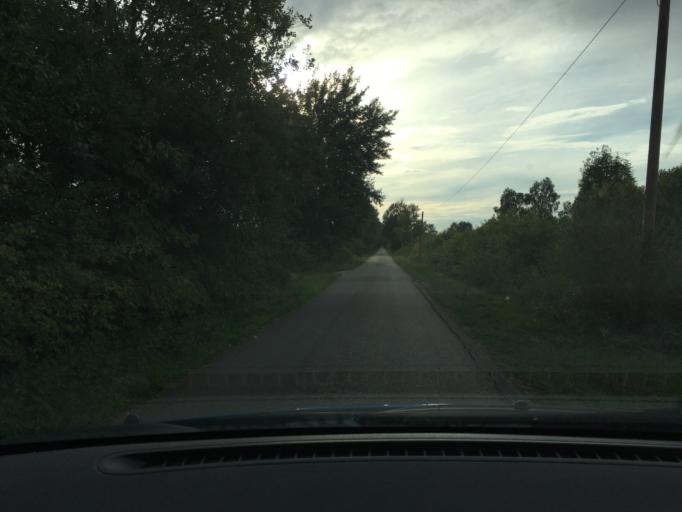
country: DE
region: Lower Saxony
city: Wietzendorf
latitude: 52.8911
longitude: 9.9414
